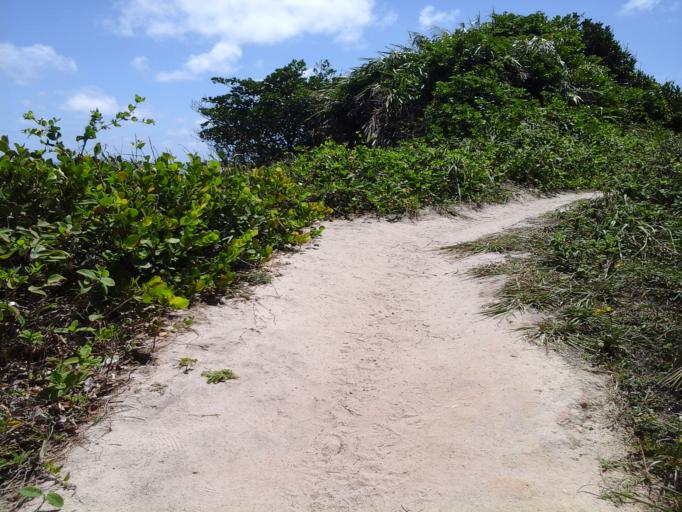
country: BR
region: Paraiba
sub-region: Pitimbu
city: Pitimbu
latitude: -7.3641
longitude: -34.7984
